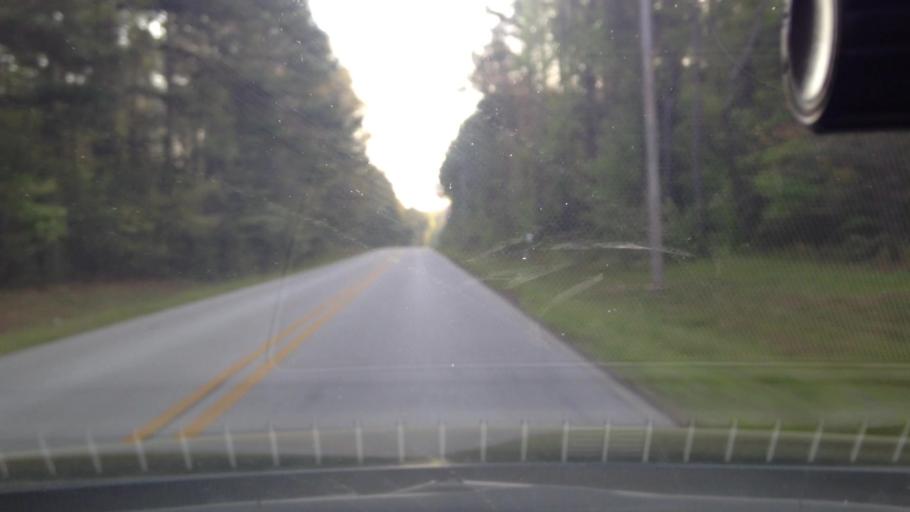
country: US
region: Georgia
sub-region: Spalding County
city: Experiment
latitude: 33.2717
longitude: -84.3353
